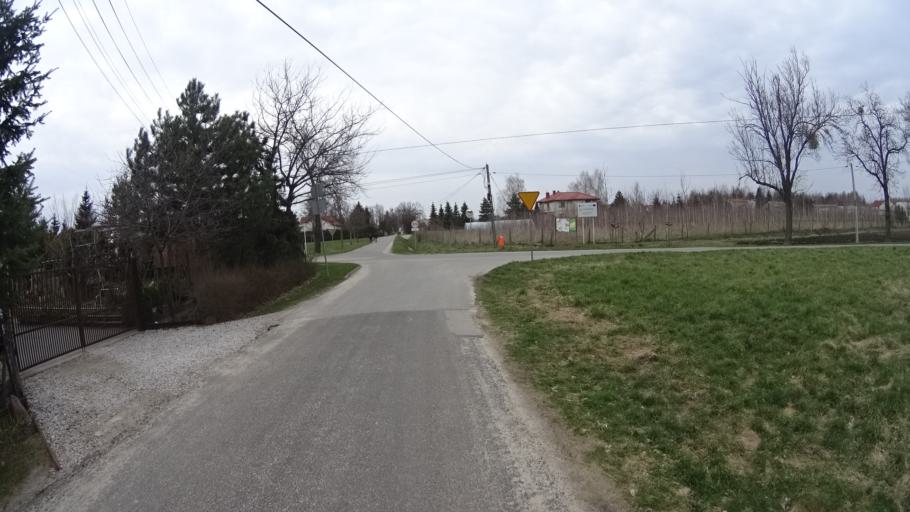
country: PL
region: Masovian Voivodeship
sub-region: Powiat warszawski zachodni
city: Jozefow
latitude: 52.2061
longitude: 20.6836
